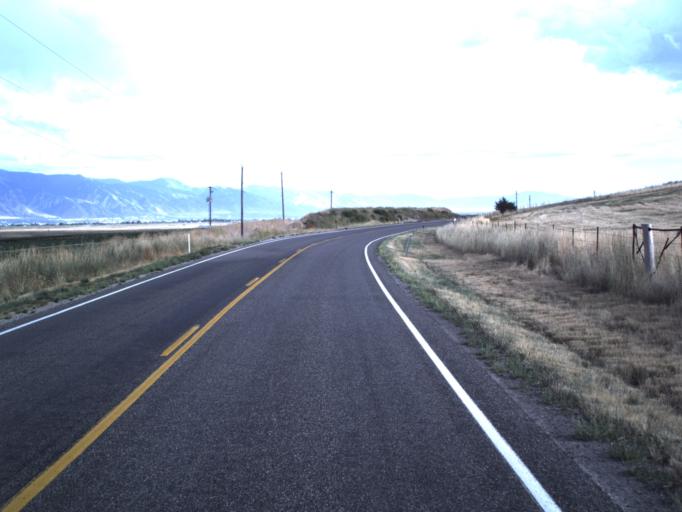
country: US
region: Utah
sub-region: Cache County
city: Benson
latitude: 41.8770
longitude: -111.9492
